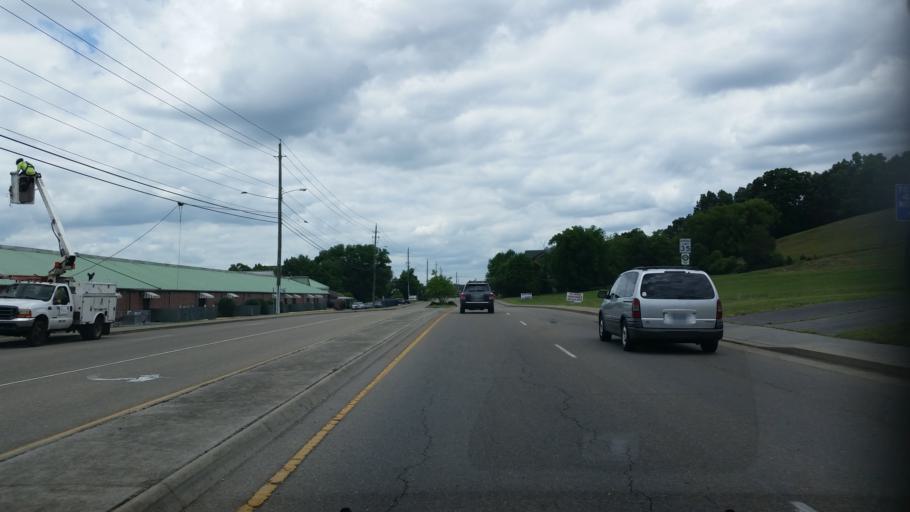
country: US
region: Tennessee
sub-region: Sevier County
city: Pigeon Forge
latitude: 35.8067
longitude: -83.5732
